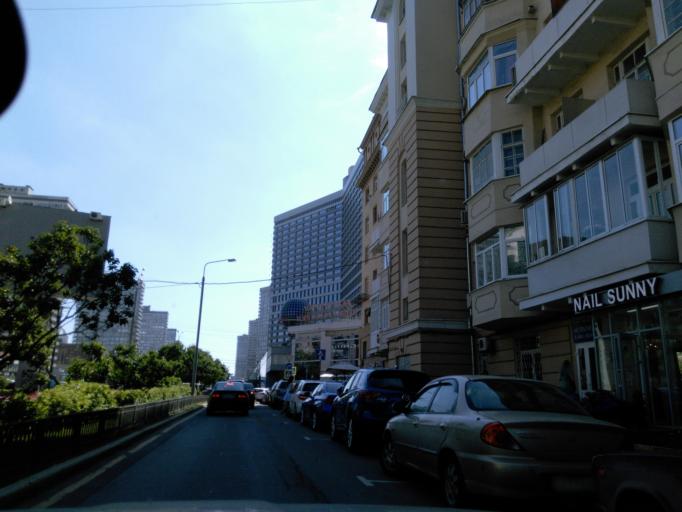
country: RU
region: Moskovskaya
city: Dorogomilovo
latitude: 55.7522
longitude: 37.5817
